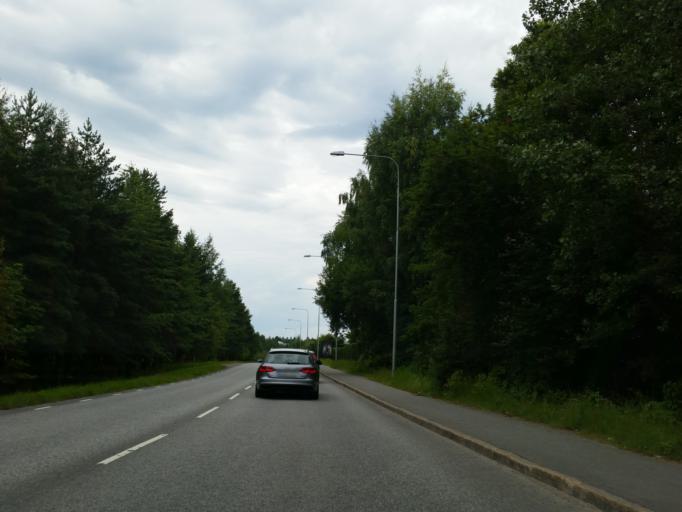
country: SE
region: Stockholm
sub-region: Sodertalje Kommun
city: Soedertaelje
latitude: 59.2020
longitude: 17.6006
